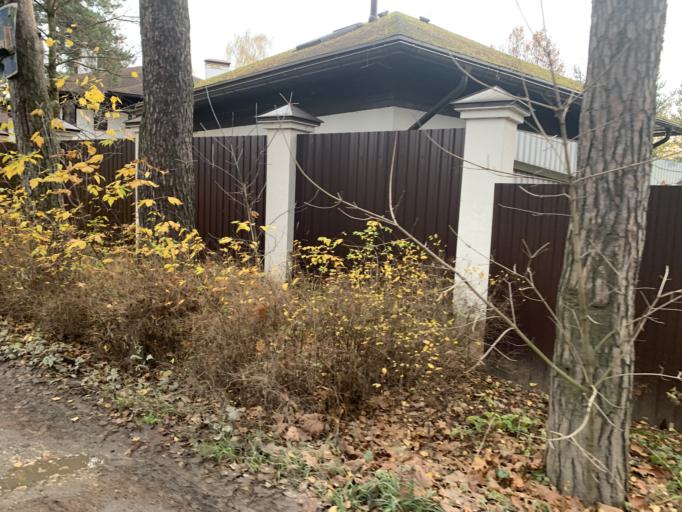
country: RU
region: Moskovskaya
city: Mamontovka
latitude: 55.9839
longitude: 37.8406
